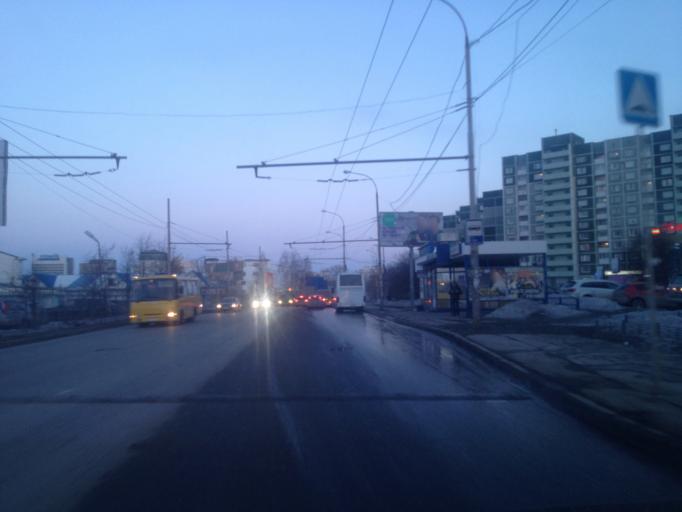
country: RU
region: Sverdlovsk
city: Yekaterinburg
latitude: 56.7946
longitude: 60.6341
